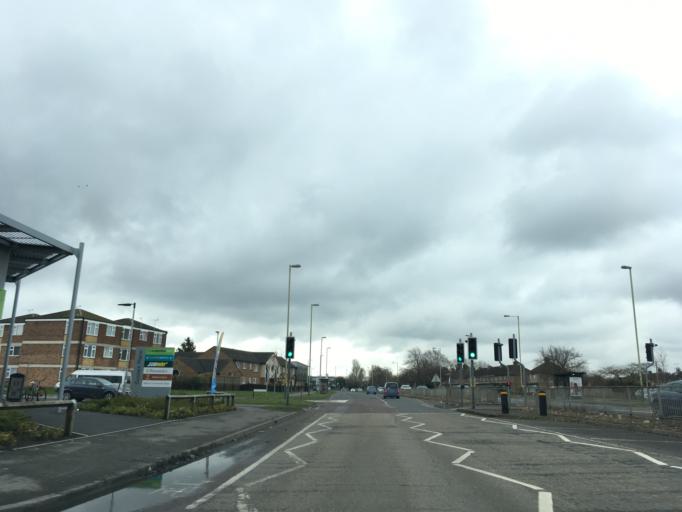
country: GB
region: England
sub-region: Borough of Swindon
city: Swindon
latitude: 51.5599
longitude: -1.7639
